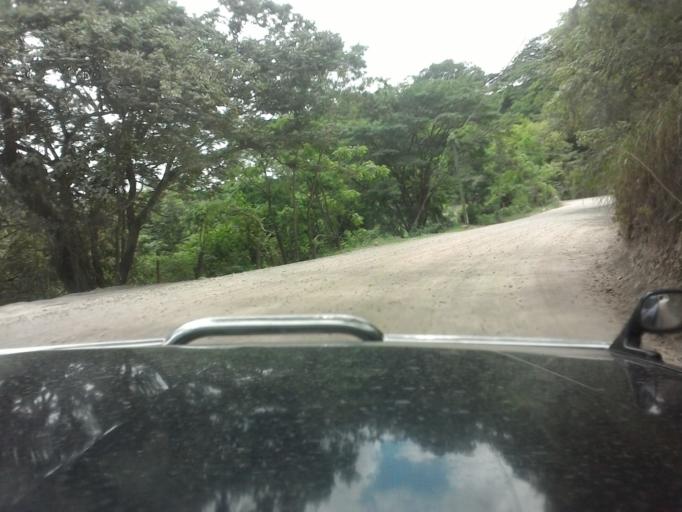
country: CR
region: Guanacaste
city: Juntas
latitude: 10.2167
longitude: -84.8542
